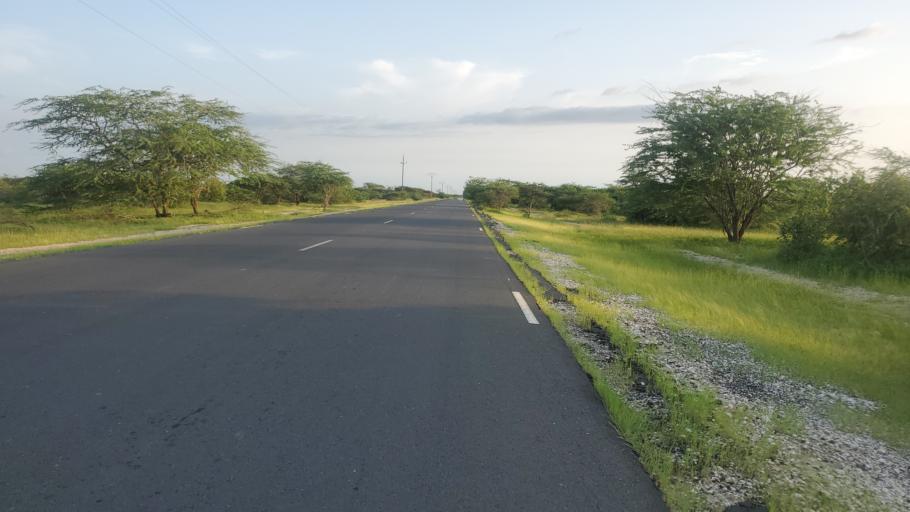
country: SN
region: Saint-Louis
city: Saint-Louis
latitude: 16.1854
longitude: -16.4094
